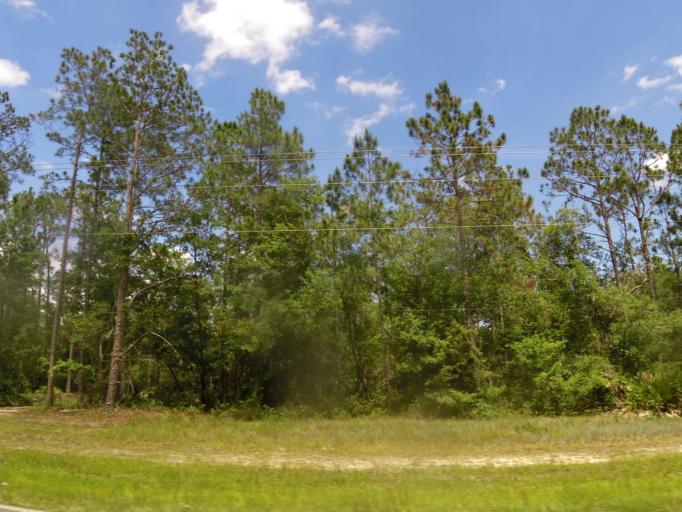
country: US
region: Florida
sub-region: Clay County
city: Green Cove Springs
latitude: 29.9898
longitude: -81.7313
